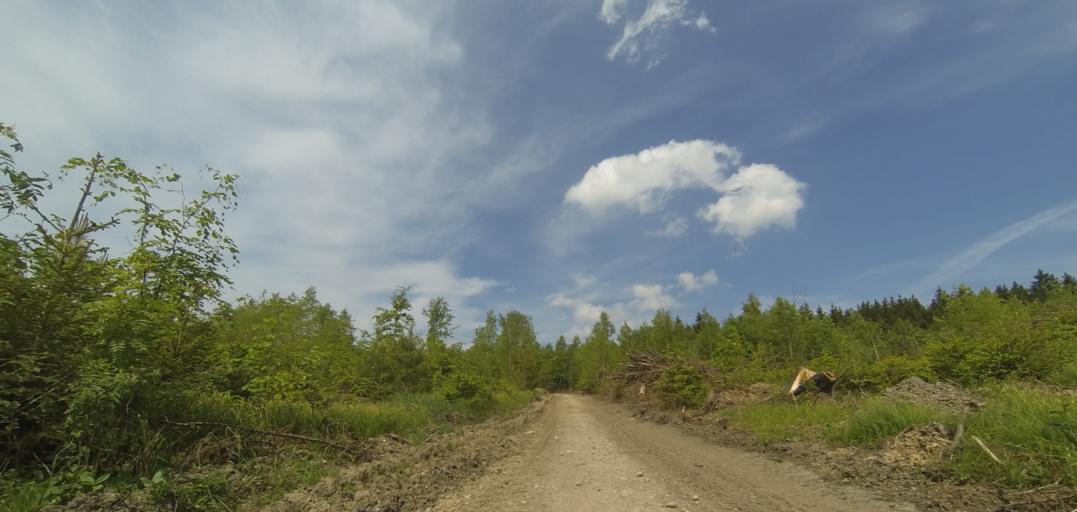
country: DE
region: Saxony
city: Grossharthau
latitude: 51.1067
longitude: 14.1223
